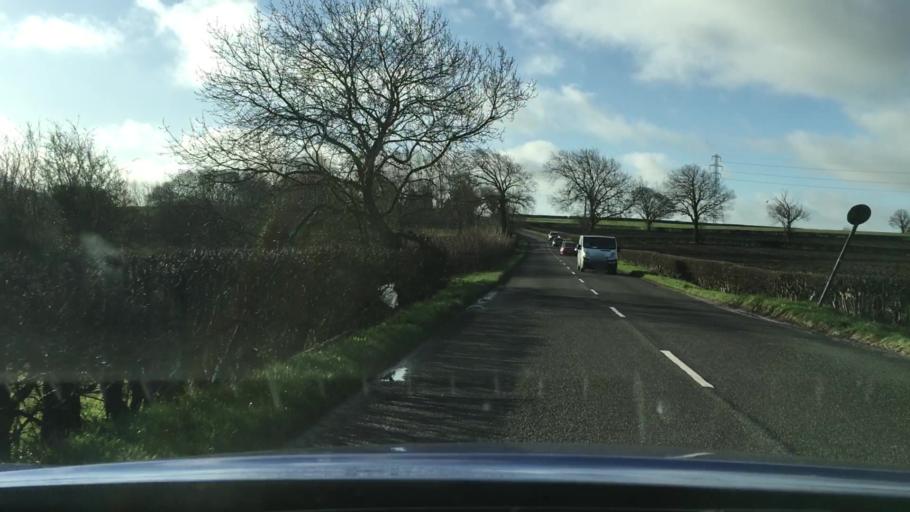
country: GB
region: England
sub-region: Derbyshire
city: Tibshelf
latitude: 53.1594
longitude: -1.3428
